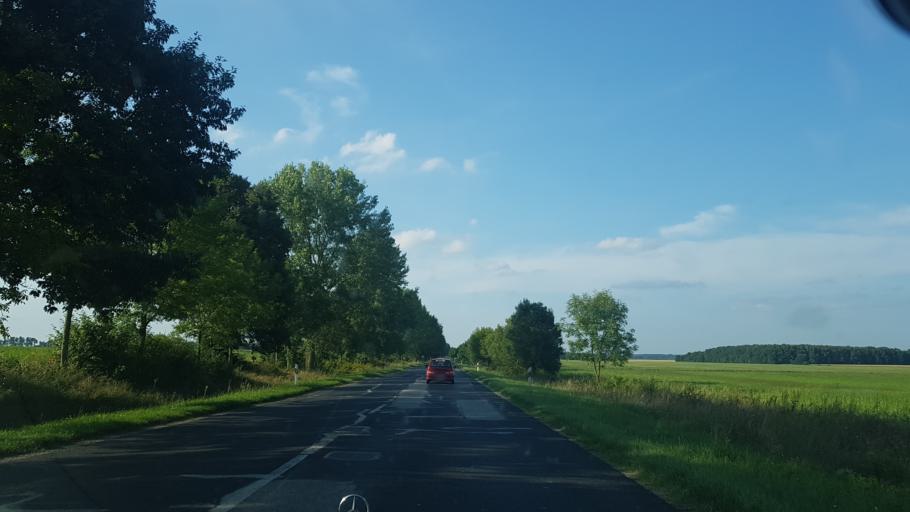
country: HU
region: Somogy
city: Nagyatad
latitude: 46.2532
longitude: 17.3561
